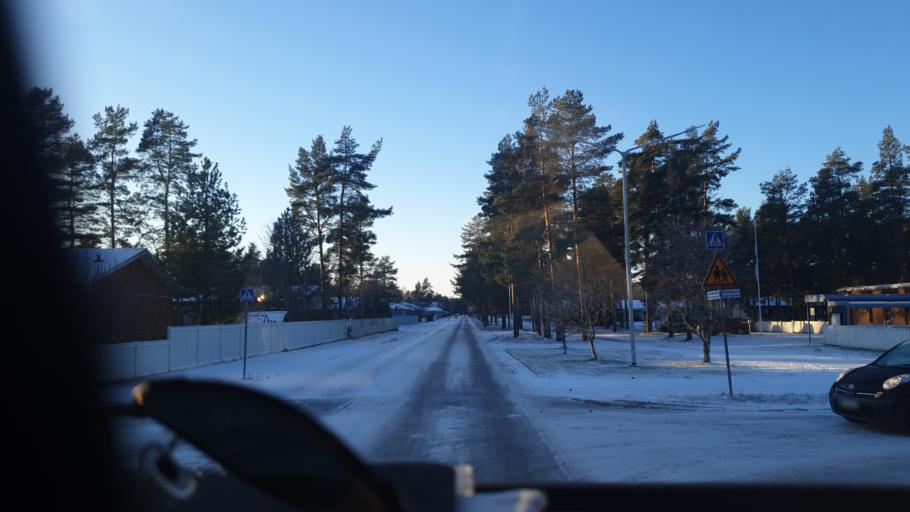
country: FI
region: Central Ostrobothnia
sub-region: Kokkola
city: Kokkola
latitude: 63.8252
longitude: 23.0857
